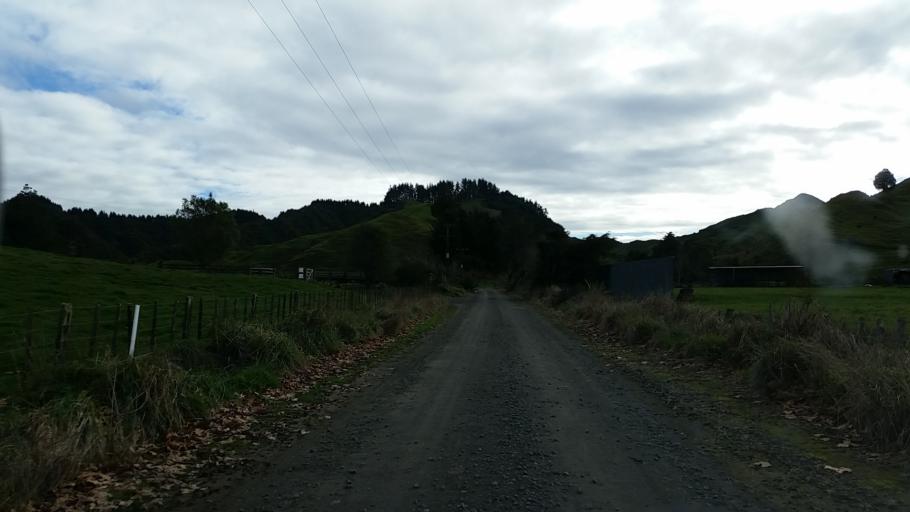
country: NZ
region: Taranaki
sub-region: South Taranaki District
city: Eltham
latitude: -39.2338
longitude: 174.5200
